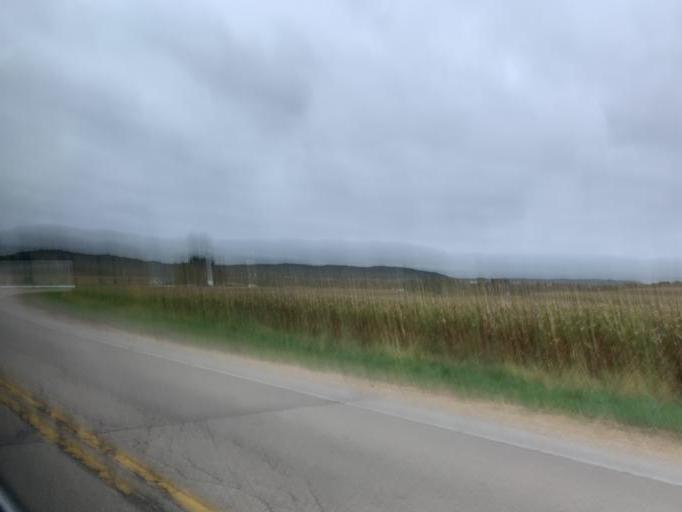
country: US
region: Wisconsin
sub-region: Grant County
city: Muscoda
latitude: 43.2177
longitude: -90.5615
